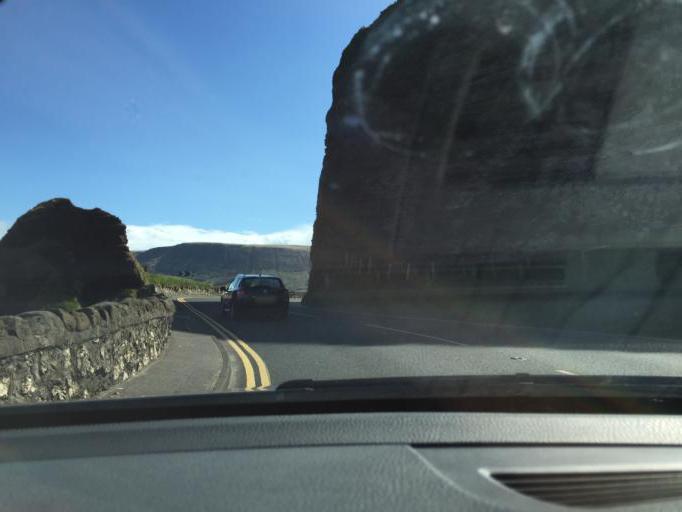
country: GB
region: Northern Ireland
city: Cushendall
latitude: 55.0678
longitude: -6.0547
